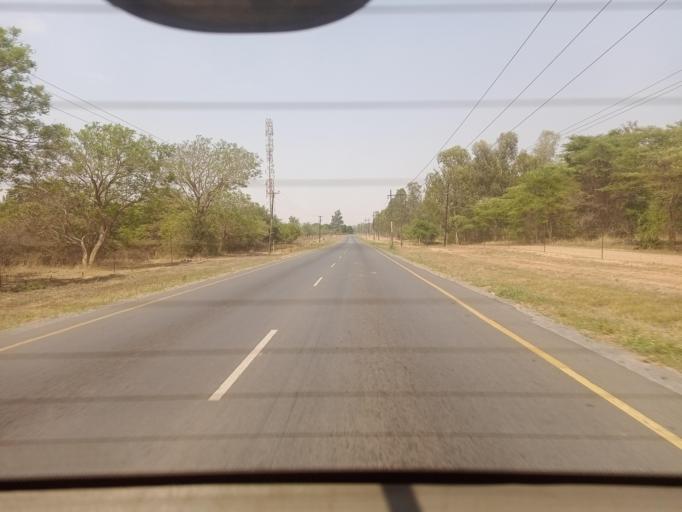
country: ZM
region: Lusaka
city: Lusaka
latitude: -15.2855
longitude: 28.3826
